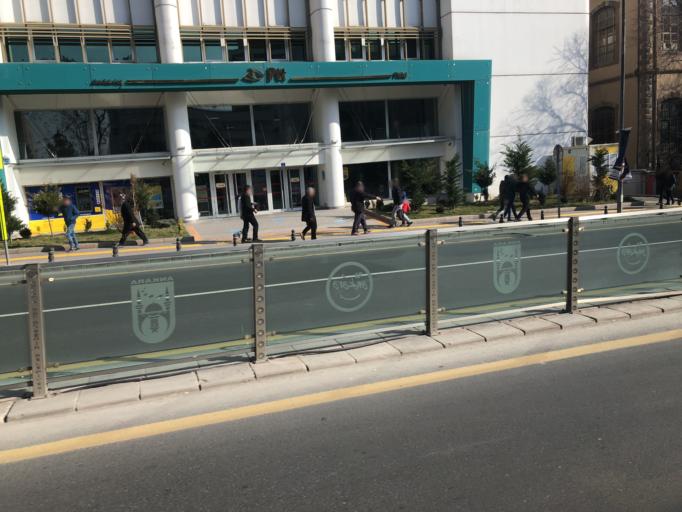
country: TR
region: Ankara
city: Ankara
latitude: 39.9403
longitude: 32.8544
